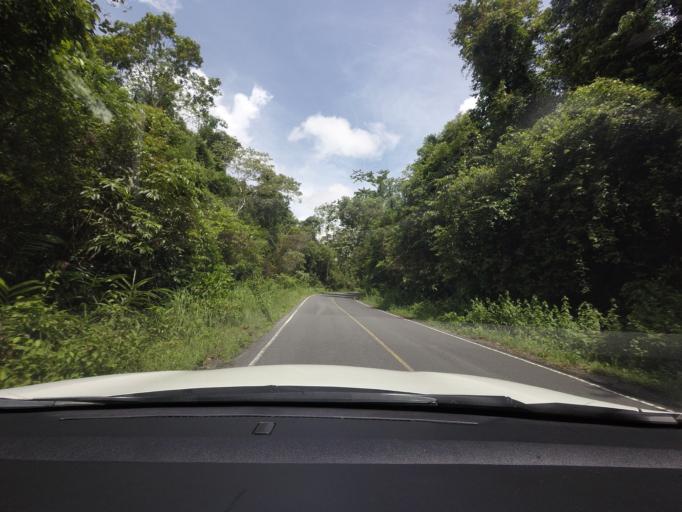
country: TH
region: Nakhon Nayok
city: Pak Phli
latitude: 14.2960
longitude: 101.3941
